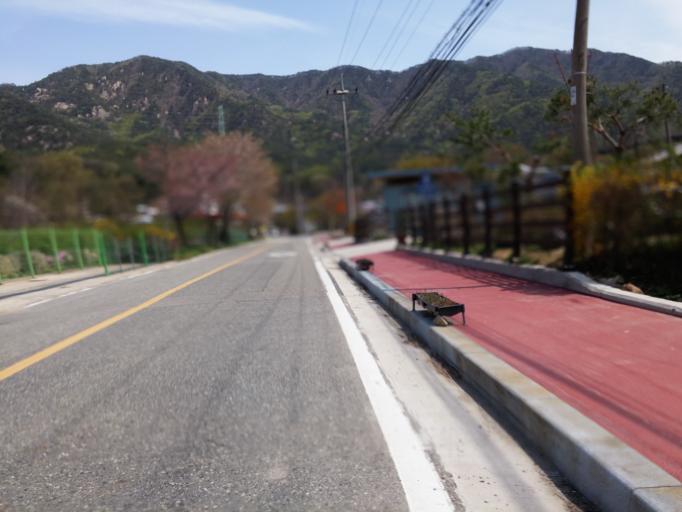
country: KR
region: Chungcheongbuk-do
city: Okcheon
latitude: 36.2505
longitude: 127.5489
